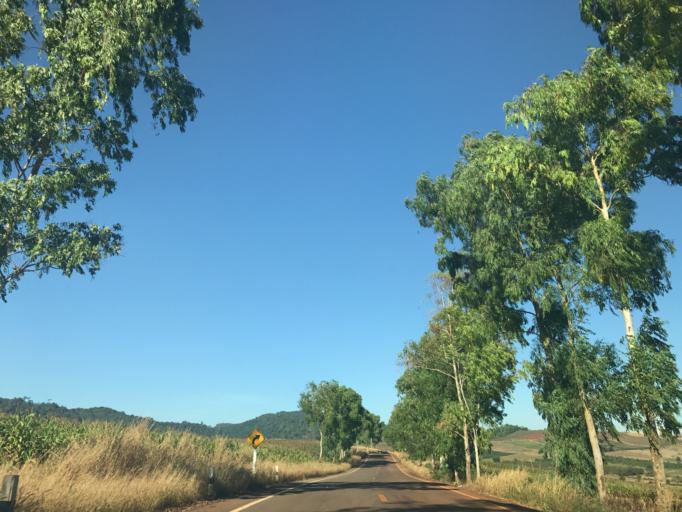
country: TH
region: Tak
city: Phop Phra
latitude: 16.5336
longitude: 98.7951
